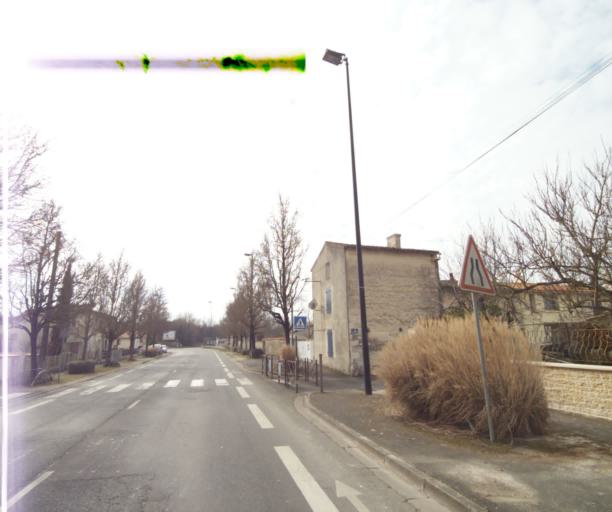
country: FR
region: Poitou-Charentes
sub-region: Departement des Deux-Sevres
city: Niort
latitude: 46.3076
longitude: -0.4657
